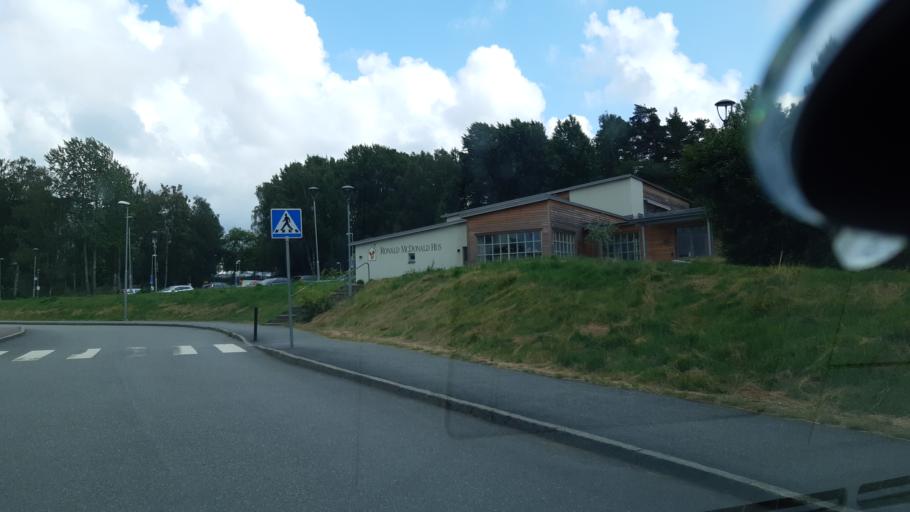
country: SE
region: Vaestra Goetaland
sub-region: Goteborg
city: Eriksbo
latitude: 57.7187
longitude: 12.0525
